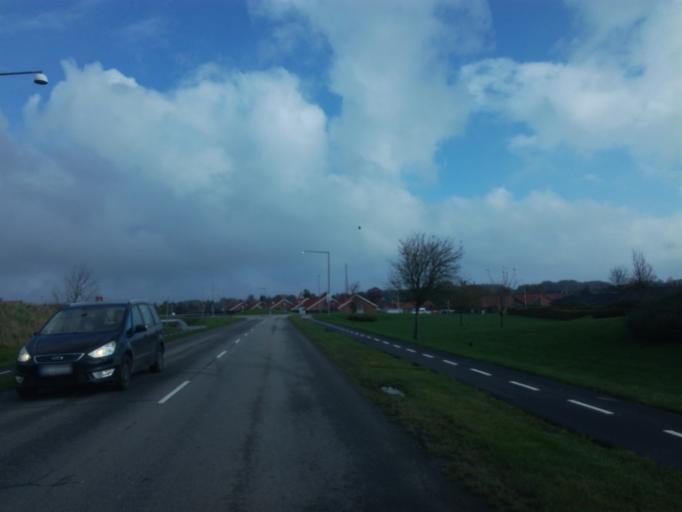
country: DK
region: South Denmark
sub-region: Vejle Kommune
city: Brejning
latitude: 55.6572
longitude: 9.6705
